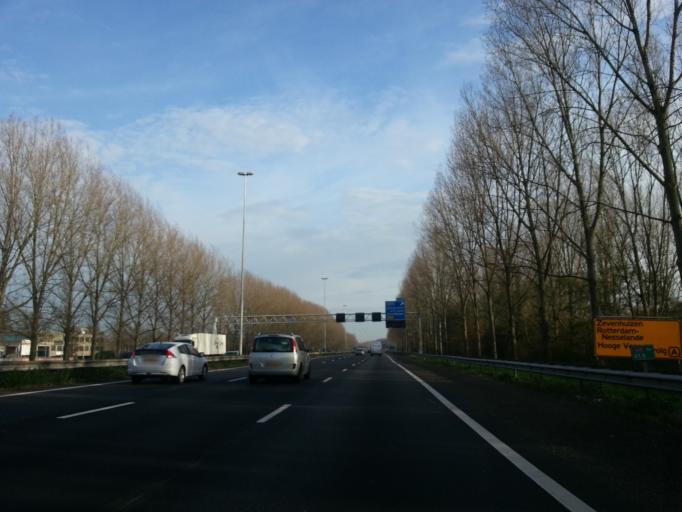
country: NL
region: South Holland
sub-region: Gemeente Capelle aan den IJssel
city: Capelle aan den IJssel
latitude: 51.9752
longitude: 4.6089
